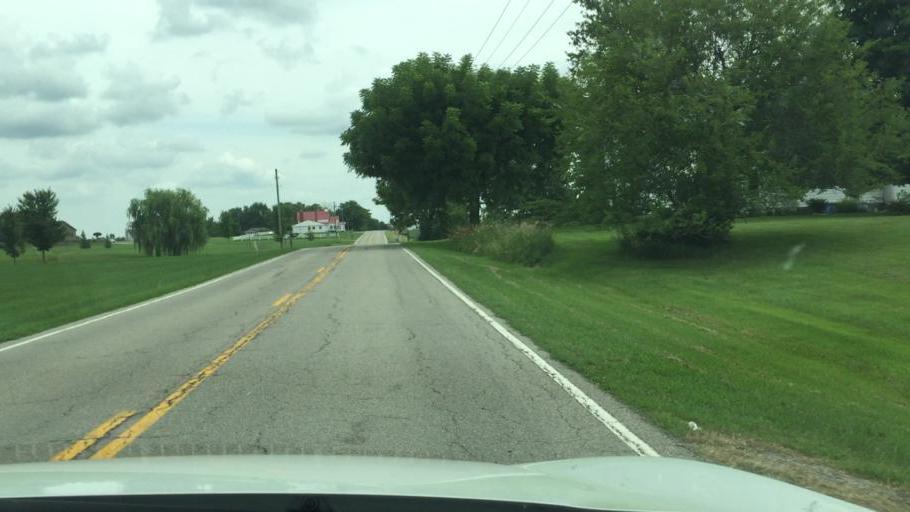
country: US
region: Ohio
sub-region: Champaign County
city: North Lewisburg
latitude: 40.2461
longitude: -83.4808
